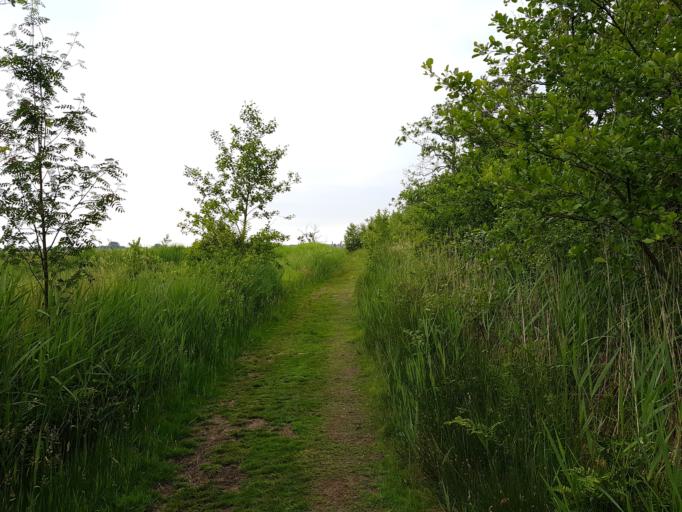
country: NL
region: Friesland
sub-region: Gemeente Boarnsterhim
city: Warten
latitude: 53.1412
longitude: 5.9304
